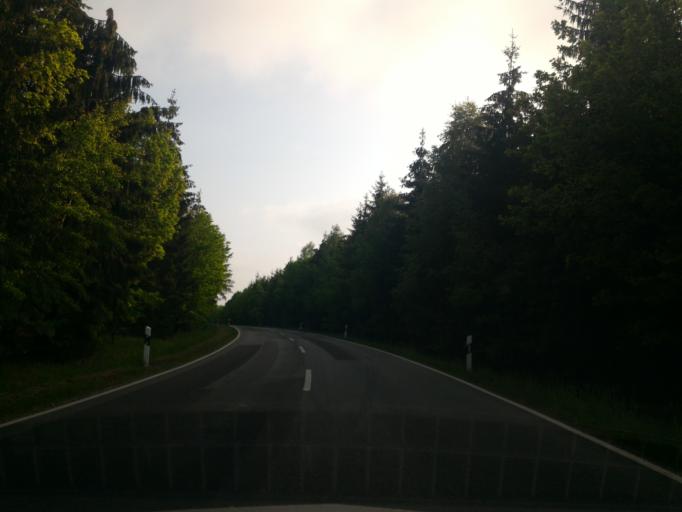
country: DE
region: Saxony
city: Leutersdorf
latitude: 50.9253
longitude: 14.6655
